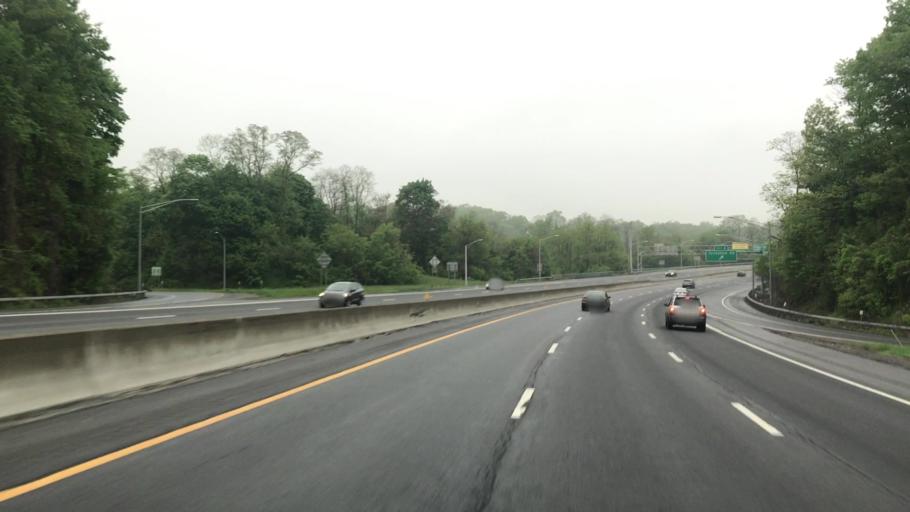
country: US
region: New York
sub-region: Westchester County
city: Bronxville
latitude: 40.9536
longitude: -73.8602
